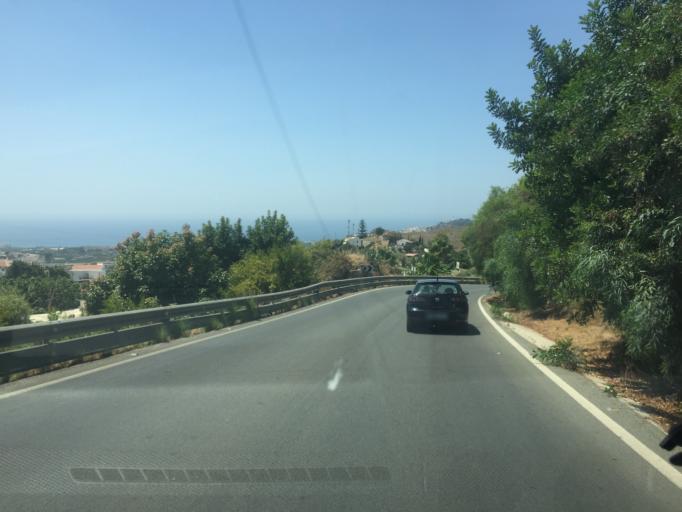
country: ES
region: Andalusia
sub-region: Provincia de Malaga
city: Frigiliana
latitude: 36.7686
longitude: -3.8917
